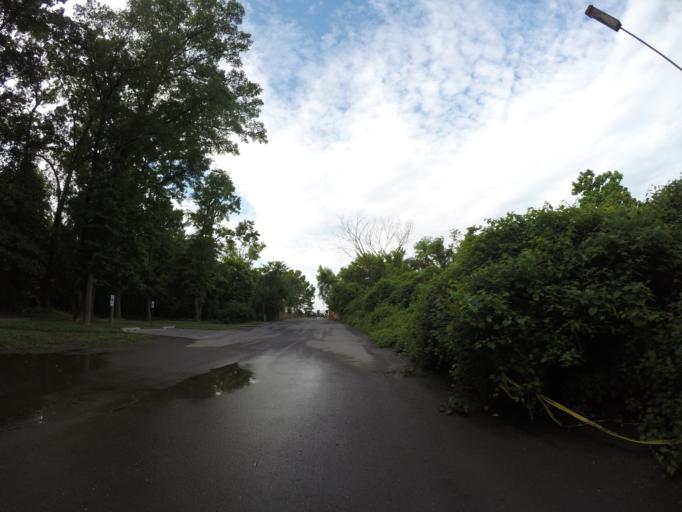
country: US
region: Maryland
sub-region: Prince George's County
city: Berwyn Heights
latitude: 38.9916
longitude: -76.9217
